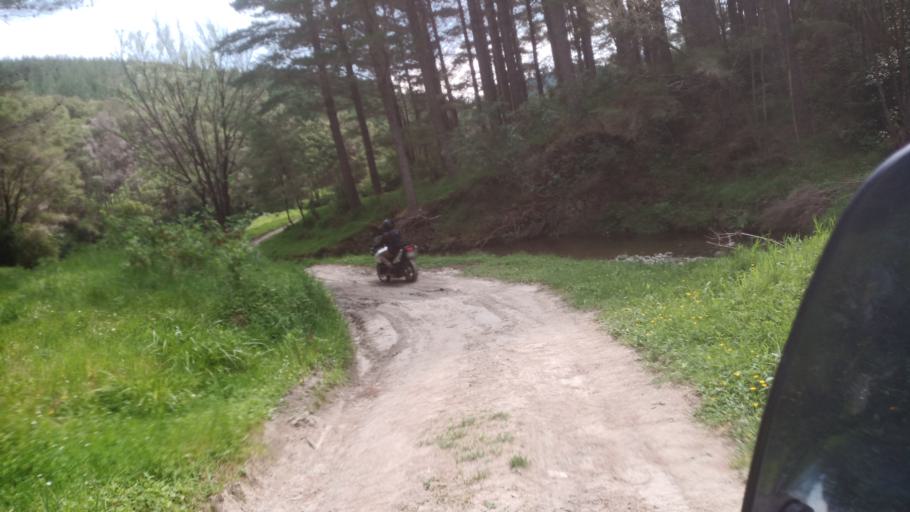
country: NZ
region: Gisborne
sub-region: Gisborne District
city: Gisborne
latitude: -38.4554
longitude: 177.9239
